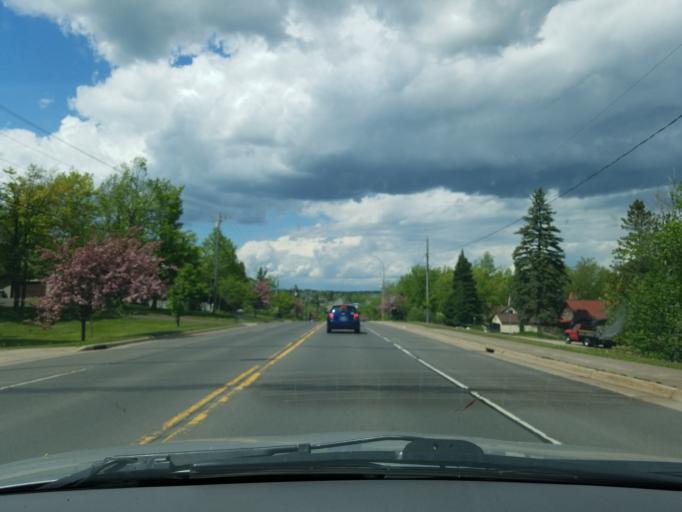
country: US
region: Minnesota
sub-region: Saint Louis County
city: Proctor
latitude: 46.7322
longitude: -92.2171
